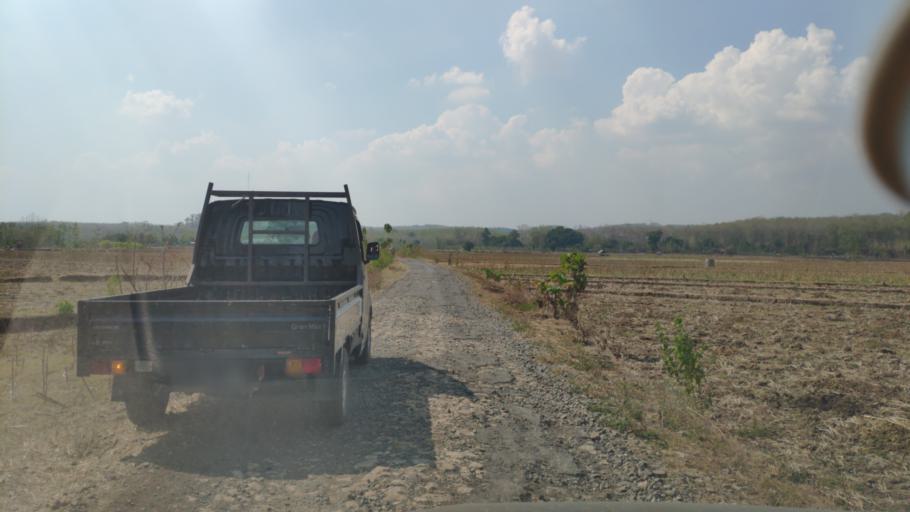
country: ID
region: Central Java
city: Botoh
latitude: -7.0867
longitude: 111.4712
